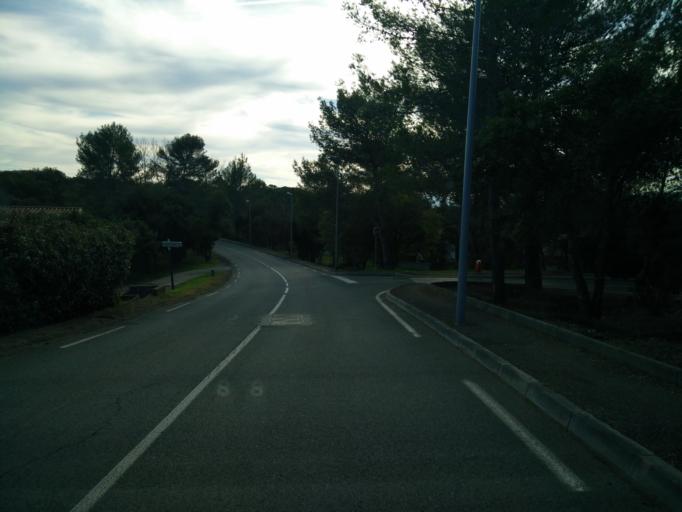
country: FR
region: Provence-Alpes-Cote d'Azur
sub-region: Departement du Var
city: Puget-sur-Argens
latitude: 43.5031
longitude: 6.6418
